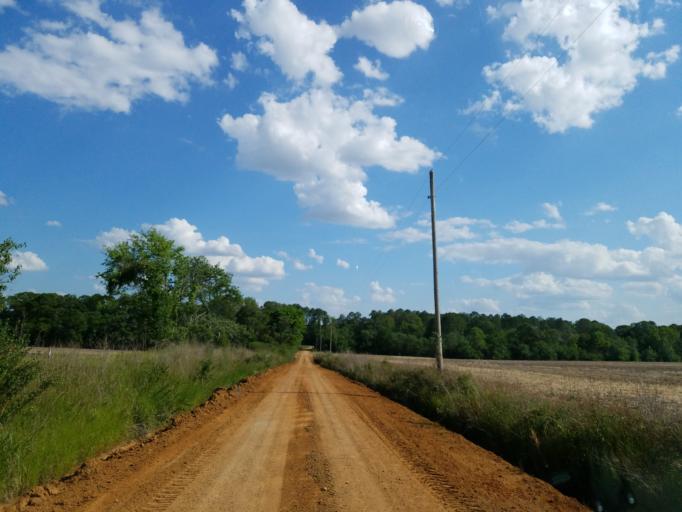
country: US
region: Georgia
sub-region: Crisp County
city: Cordele
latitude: 31.9938
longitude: -83.7406
